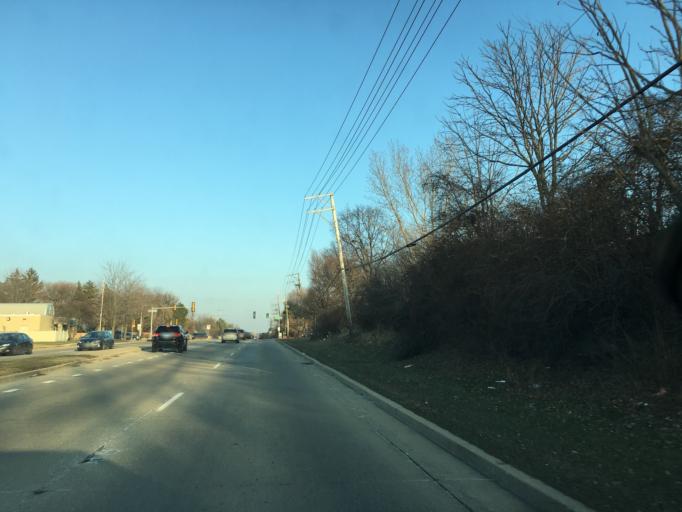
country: US
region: Illinois
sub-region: Kane County
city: Aurora
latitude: 41.7412
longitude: -88.2440
